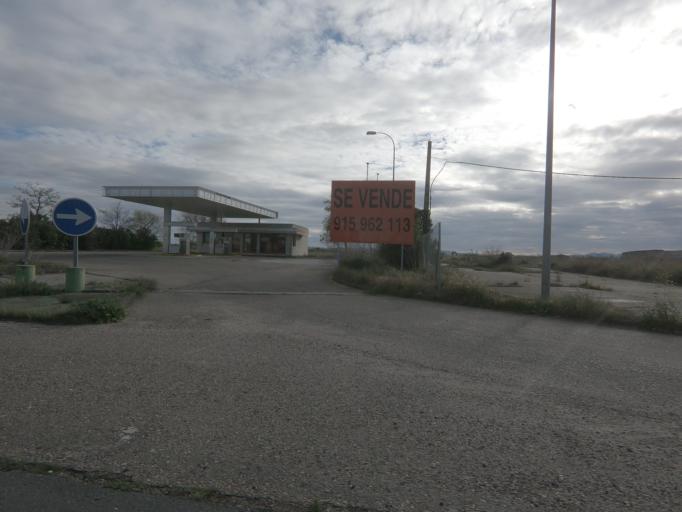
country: ES
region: Extremadura
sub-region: Provincia de Caceres
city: Moraleja
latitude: 40.0565
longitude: -6.6450
